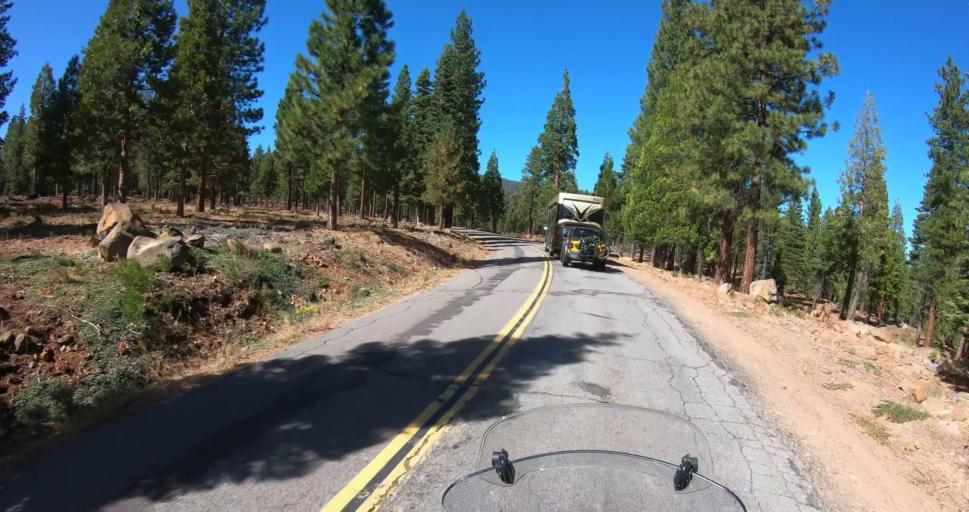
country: US
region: California
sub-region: Lassen County
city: Susanville
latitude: 40.4468
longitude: -120.7586
